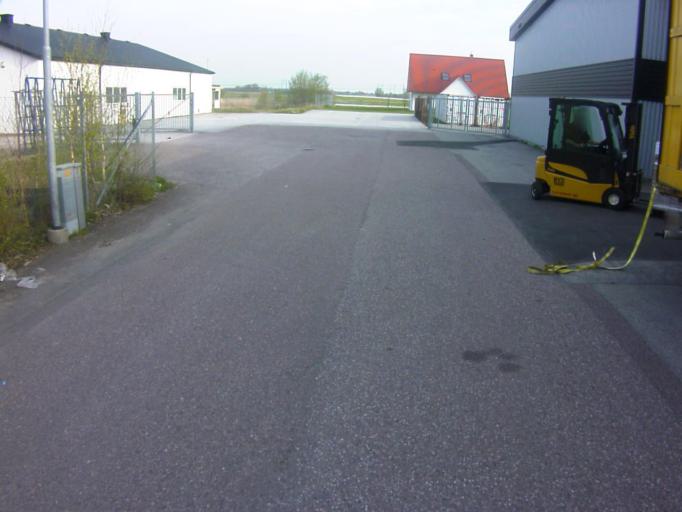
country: SE
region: Skane
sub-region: Kavlinge Kommun
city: Loddekopinge
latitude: 55.7734
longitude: 12.9999
